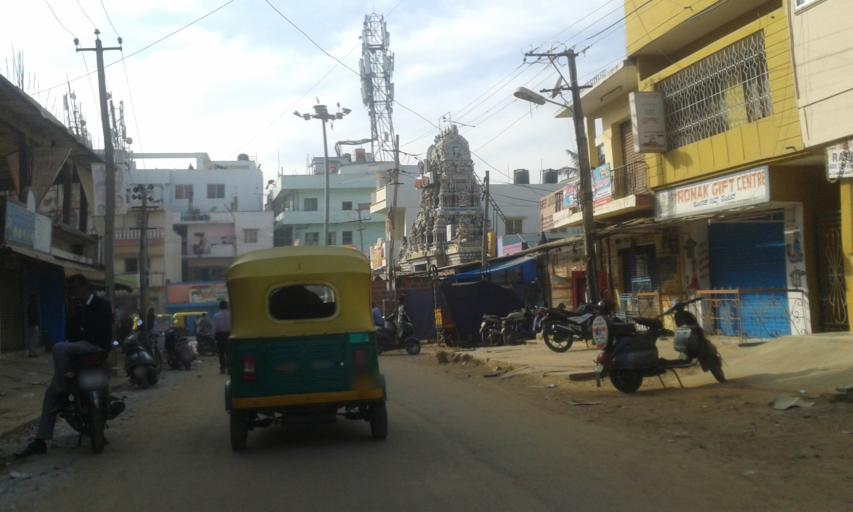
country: IN
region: Karnataka
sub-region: Bangalore Urban
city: Bangalore
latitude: 12.9571
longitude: 77.6190
